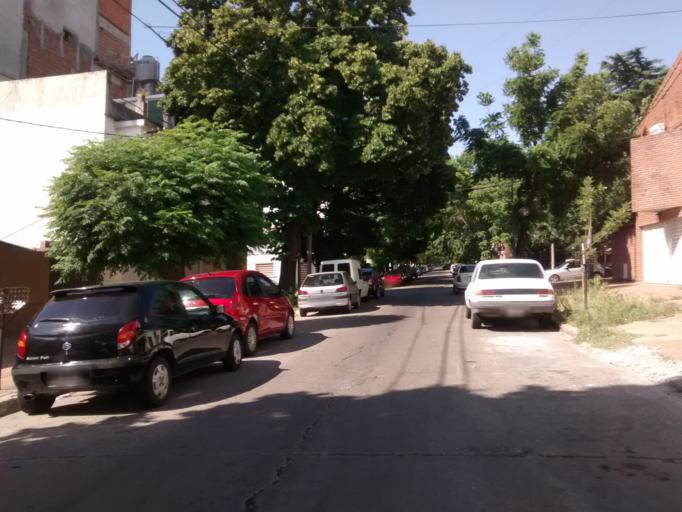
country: AR
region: Buenos Aires
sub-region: Partido de La Plata
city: La Plata
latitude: -34.9016
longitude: -57.9660
